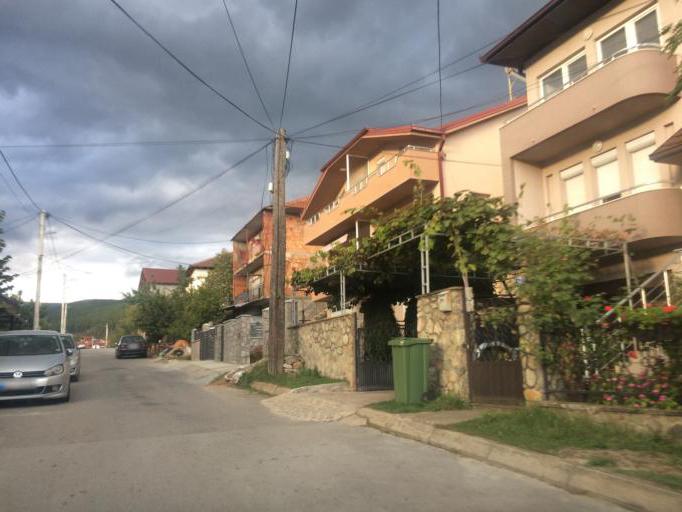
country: MK
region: Makedonska Kamenica
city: Makedonska Kamenica
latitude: 42.0172
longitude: 22.5918
